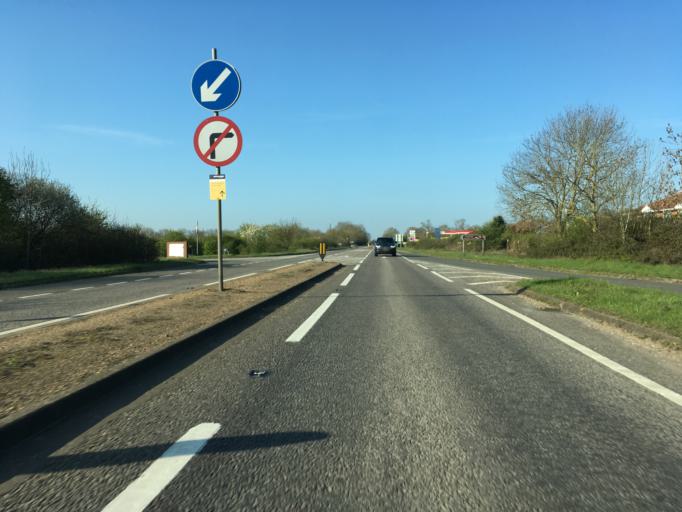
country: GB
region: England
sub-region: Northamptonshire
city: Deanshanger
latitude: 52.0435
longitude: -0.8847
